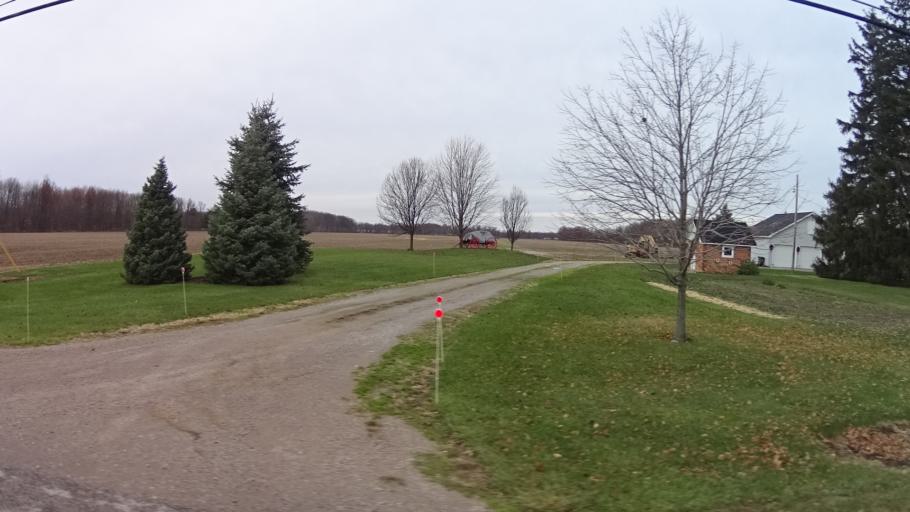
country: US
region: Ohio
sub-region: Lorain County
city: North Ridgeville
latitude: 41.3669
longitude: -82.0190
